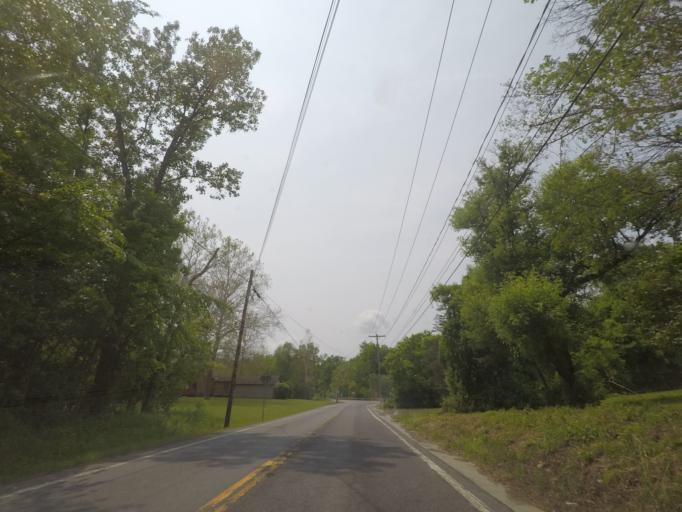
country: US
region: New York
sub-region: Rensselaer County
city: East Greenbush
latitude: 42.5499
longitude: -73.6878
